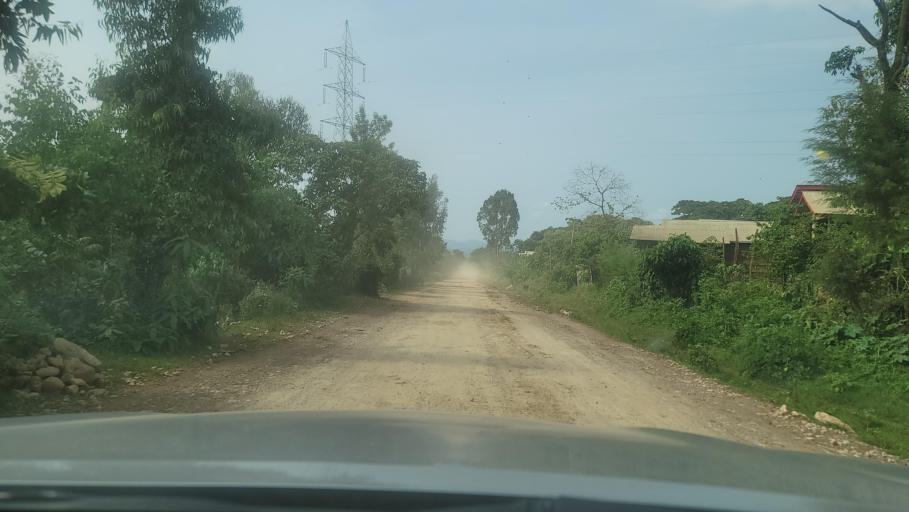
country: ET
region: Oromiya
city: Agaro
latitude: 7.8543
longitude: 36.5683
